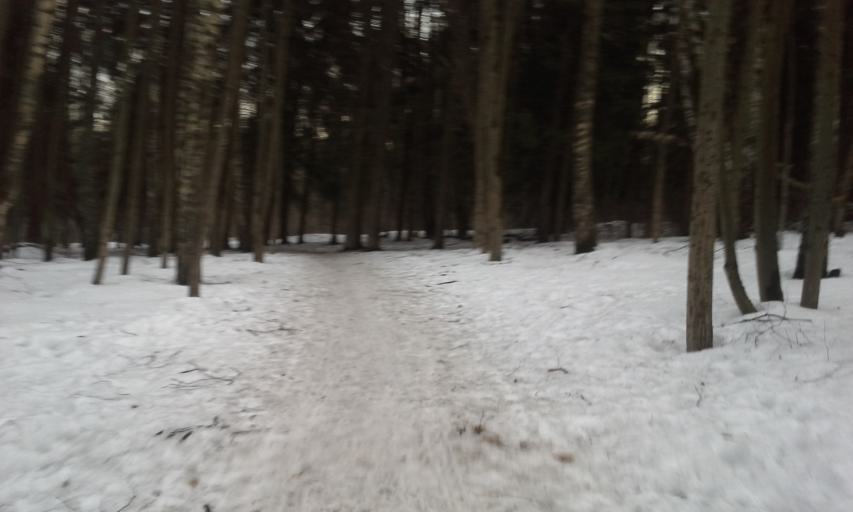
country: RU
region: Moscow
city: Zyuzino
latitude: 55.6398
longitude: 37.5758
